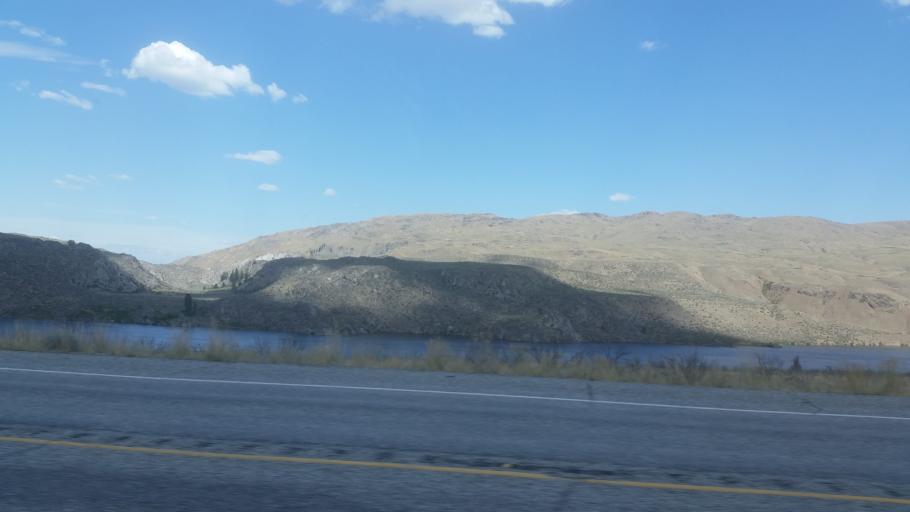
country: US
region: Washington
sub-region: Okanogan County
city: Brewster
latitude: 48.0314
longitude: -119.8936
